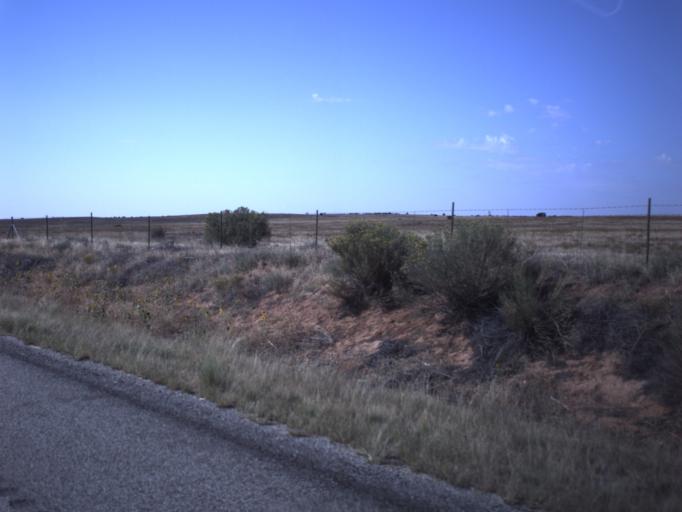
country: US
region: Utah
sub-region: San Juan County
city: Blanding
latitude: 37.4491
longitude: -109.4671
